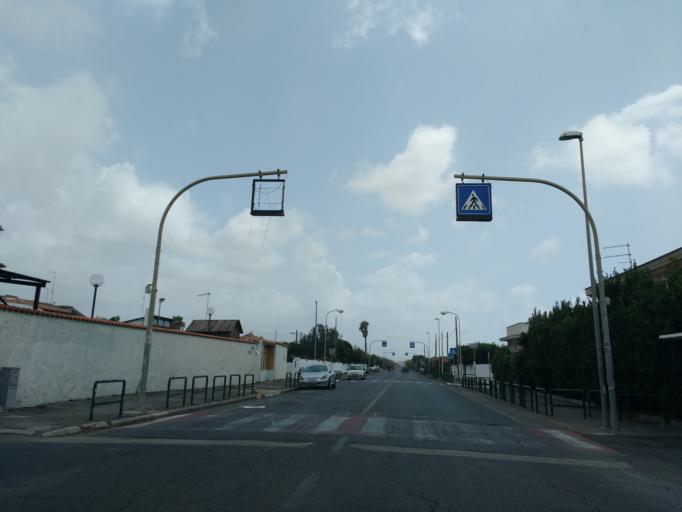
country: IT
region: Latium
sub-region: Citta metropolitana di Roma Capitale
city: Torvaianica
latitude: 41.6566
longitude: 12.4171
